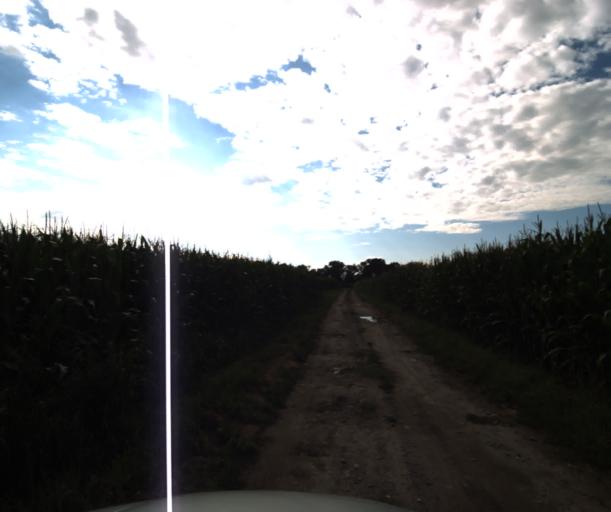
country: FR
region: Midi-Pyrenees
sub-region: Departement de la Haute-Garonne
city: Saubens
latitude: 43.4847
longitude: 1.3471
